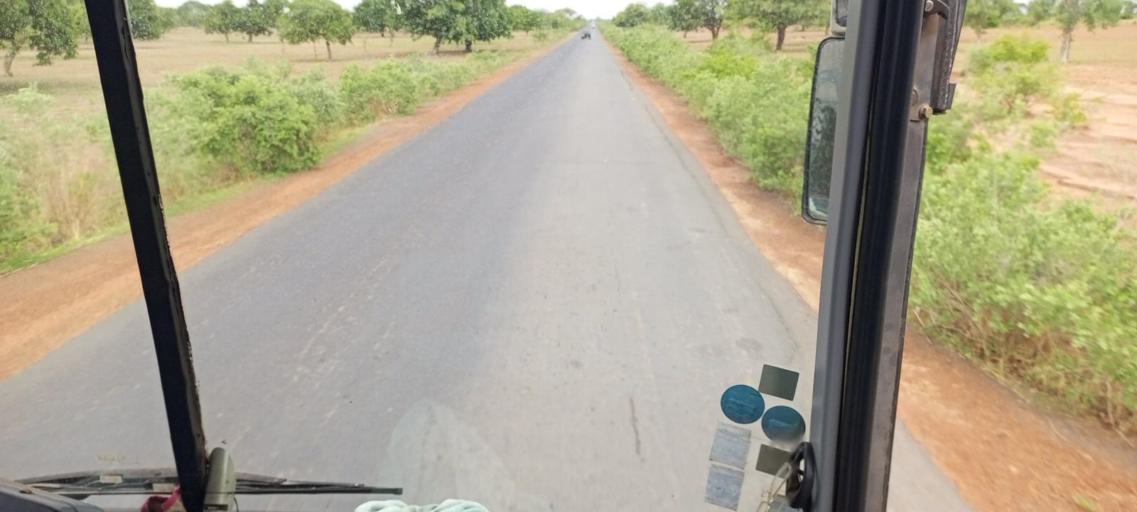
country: ML
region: Segou
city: Bla
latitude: 12.7658
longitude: -5.7406
